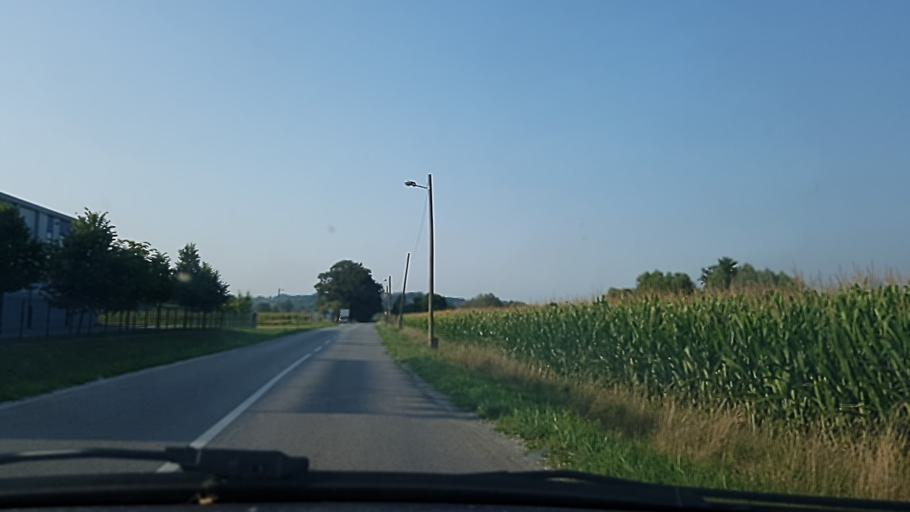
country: HR
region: Zagrebacka
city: Pojatno
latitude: 45.9402
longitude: 15.8121
